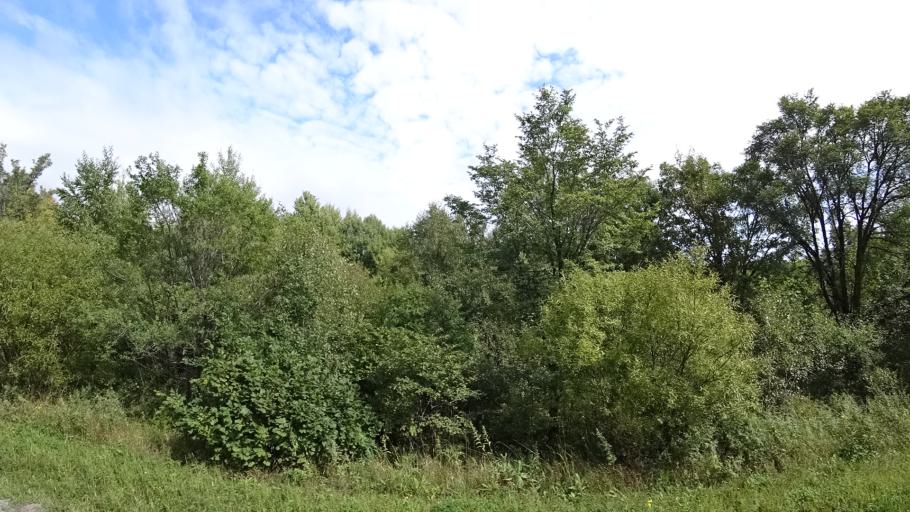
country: RU
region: Primorskiy
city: Lyalichi
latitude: 44.1476
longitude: 132.3902
